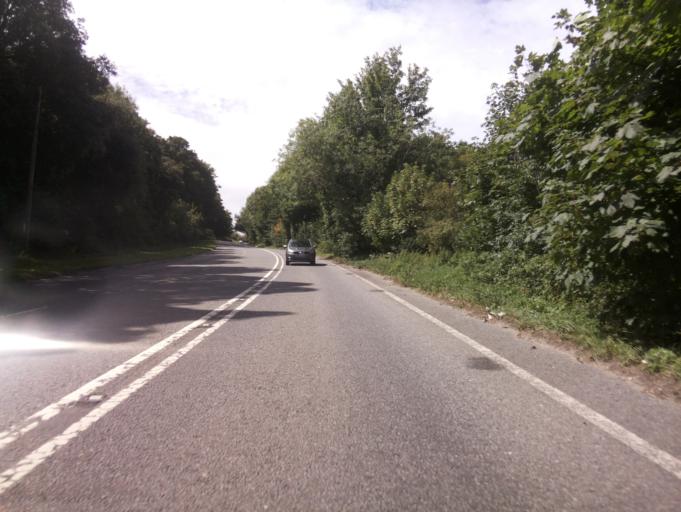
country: GB
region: England
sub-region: Dorset
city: Dorchester
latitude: 50.7646
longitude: -2.5297
